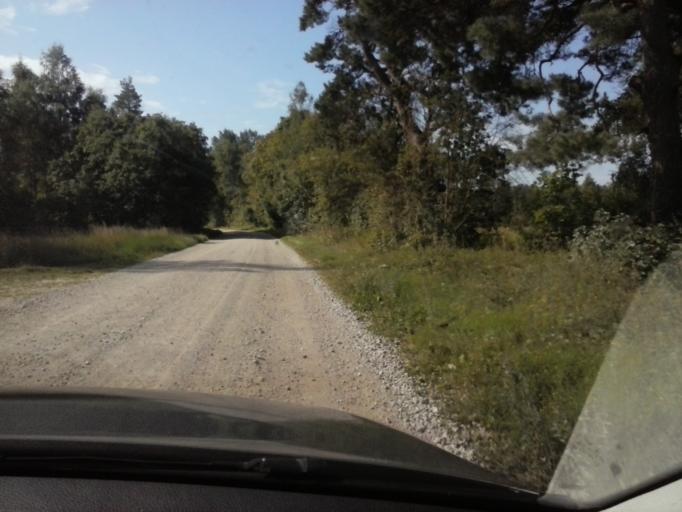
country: EE
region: Laeaene
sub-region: Haapsalu linn
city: Haapsalu
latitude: 58.8788
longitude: 23.5589
